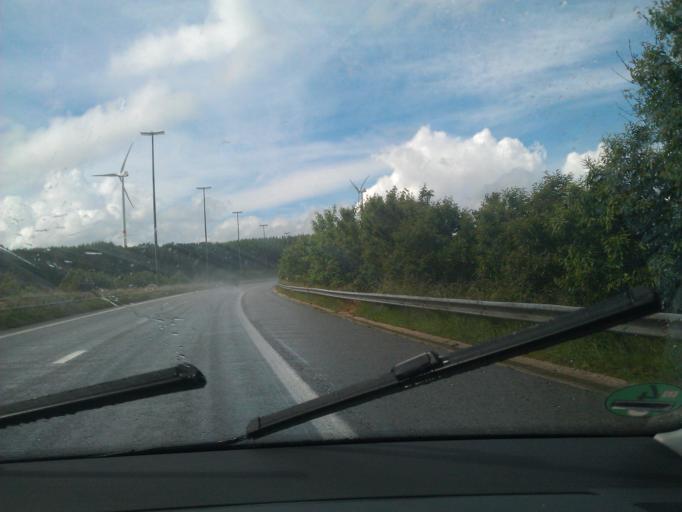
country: BE
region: Wallonia
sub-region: Province de Liege
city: Saint-Vith
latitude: 50.2983
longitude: 6.0815
